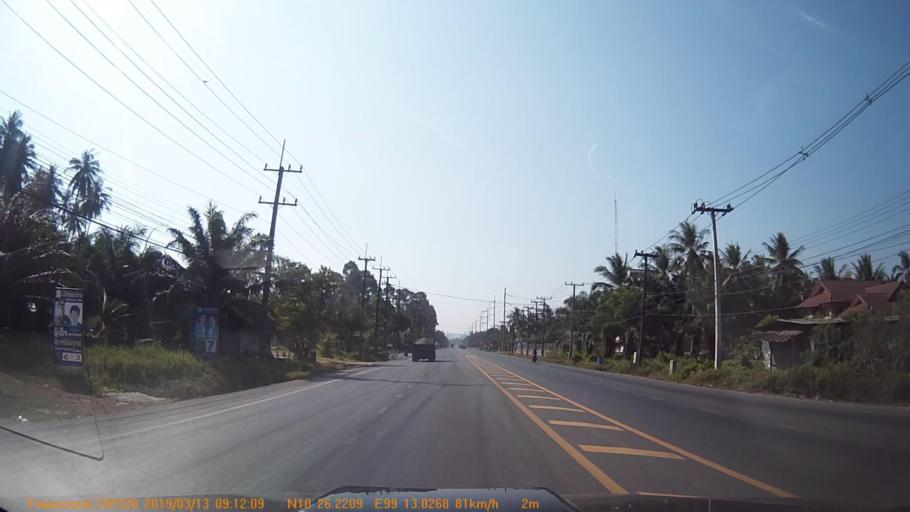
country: TH
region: Chumphon
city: Chumphon
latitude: 10.4368
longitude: 99.2172
